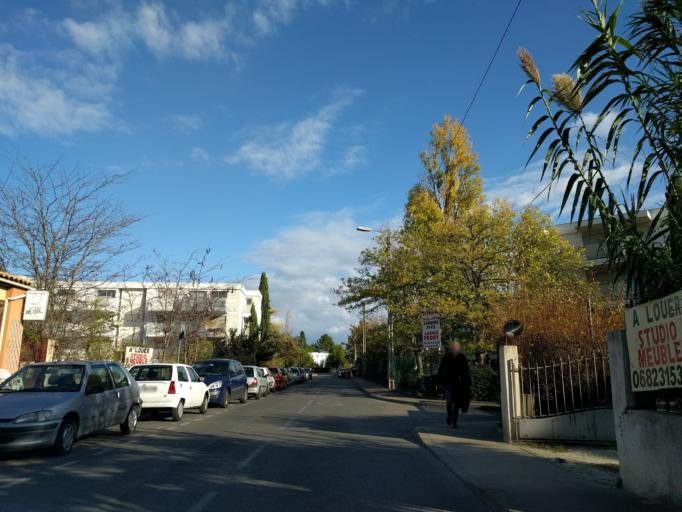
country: FR
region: Languedoc-Roussillon
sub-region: Departement de l'Herault
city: Montpellier
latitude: 43.6322
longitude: 3.8549
